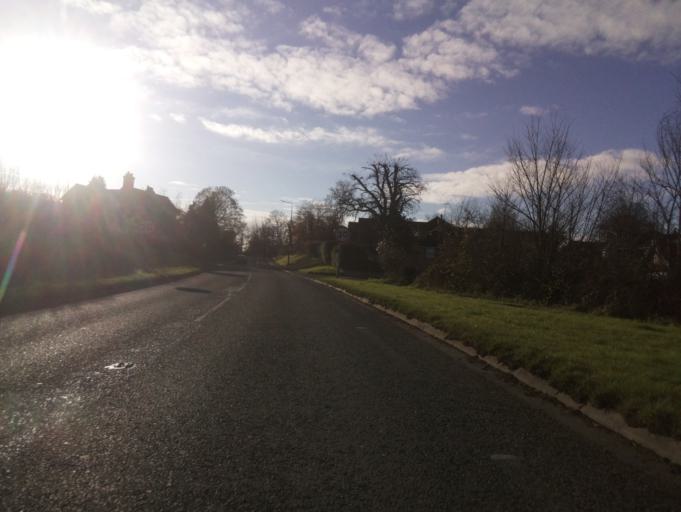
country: GB
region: England
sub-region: Derbyshire
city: Etwall
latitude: 52.8873
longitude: -1.5977
